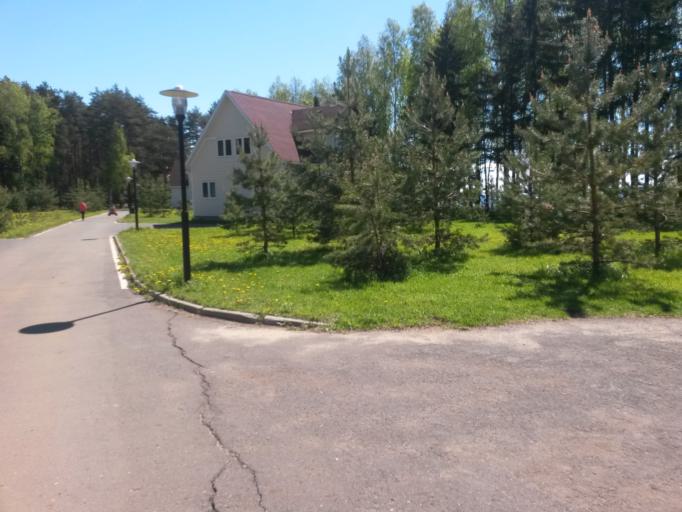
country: RU
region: Jaroslavl
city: Borok
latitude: 58.0637
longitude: 38.3408
